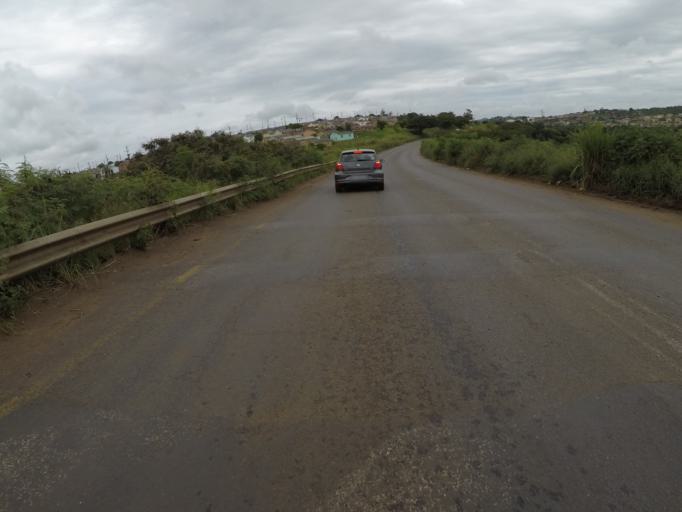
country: ZA
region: KwaZulu-Natal
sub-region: uThungulu District Municipality
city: Empangeni
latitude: -28.7656
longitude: 31.8761
